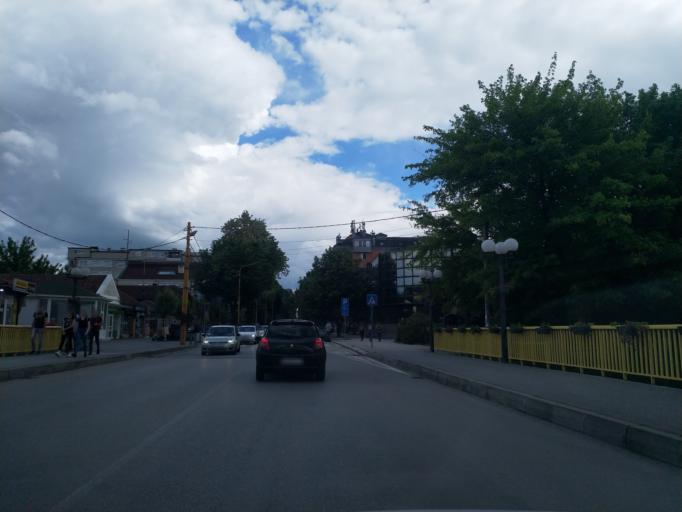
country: RS
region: Central Serbia
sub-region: Pomoravski Okrug
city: Cuprija
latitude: 43.9298
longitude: 21.3716
